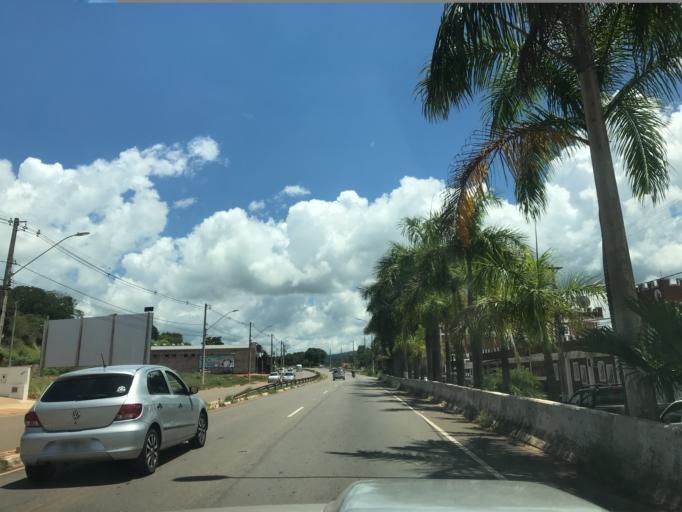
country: BR
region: Minas Gerais
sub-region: Tres Coracoes
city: Tres Coracoes
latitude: -21.6702
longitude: -45.2730
